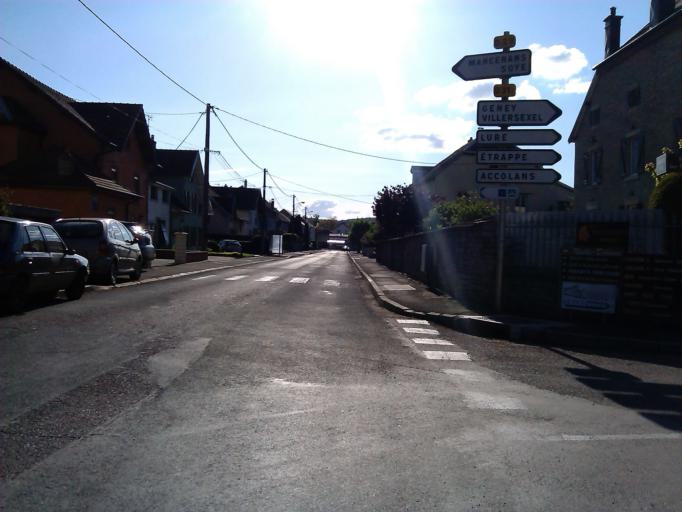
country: FR
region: Franche-Comte
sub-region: Departement du Doubs
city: Clerval
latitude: 47.4423
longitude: 6.5656
